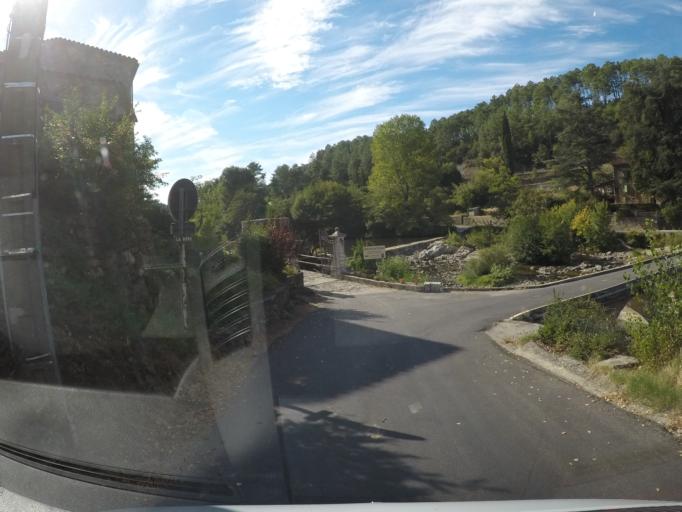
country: FR
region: Languedoc-Roussillon
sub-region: Departement du Gard
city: Anduze
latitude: 44.0747
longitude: 3.9627
